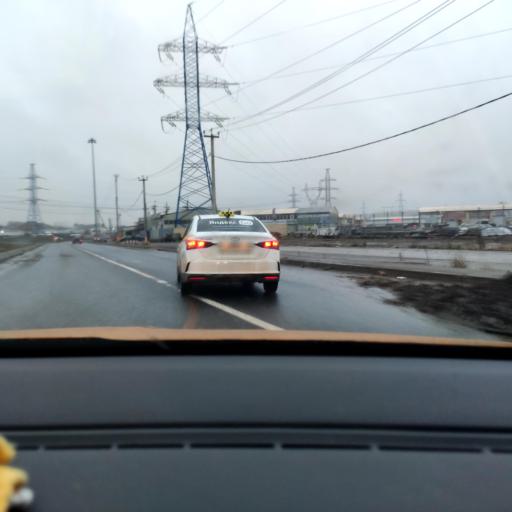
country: RU
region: Moskovskaya
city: Mosrentgen
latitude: 55.6289
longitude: 37.4347
